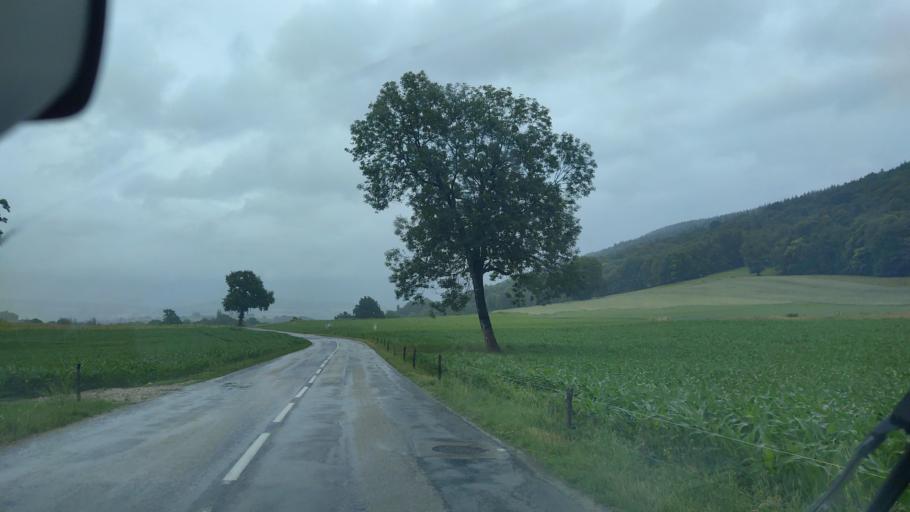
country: FR
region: Rhone-Alpes
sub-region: Departement de la Savoie
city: La Biolle
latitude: 45.7741
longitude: 5.8944
